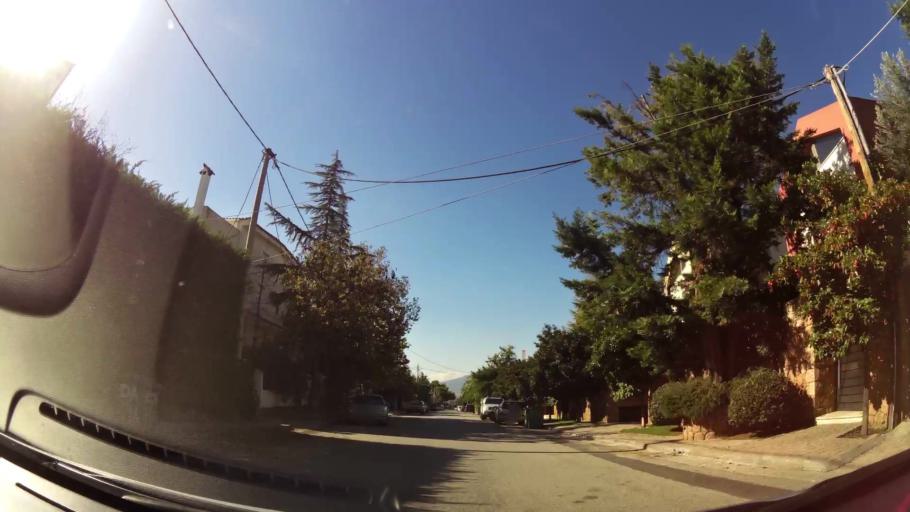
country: GR
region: Attica
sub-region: Nomarchia Athinas
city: Nea Erythraia
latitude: 38.1024
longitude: 23.8227
